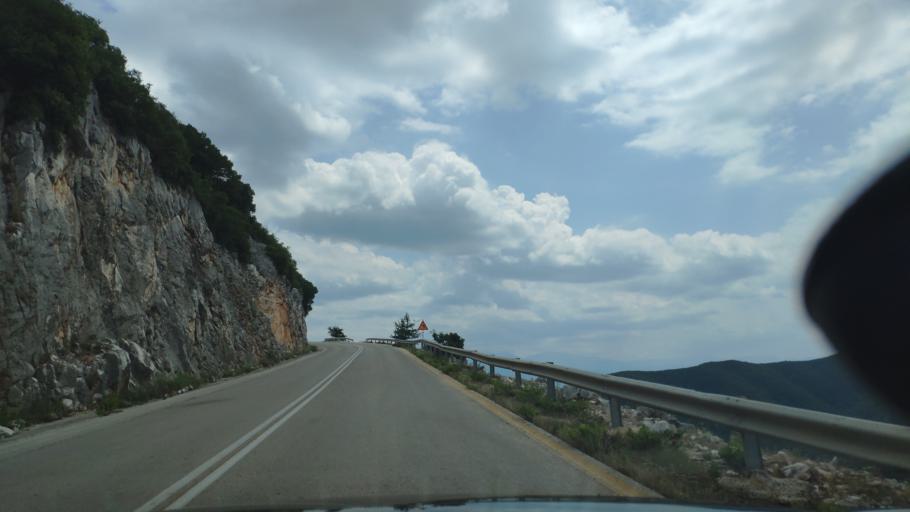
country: GR
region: Epirus
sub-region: Nomos Artas
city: Grammenitsa
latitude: 39.2759
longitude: 20.9727
